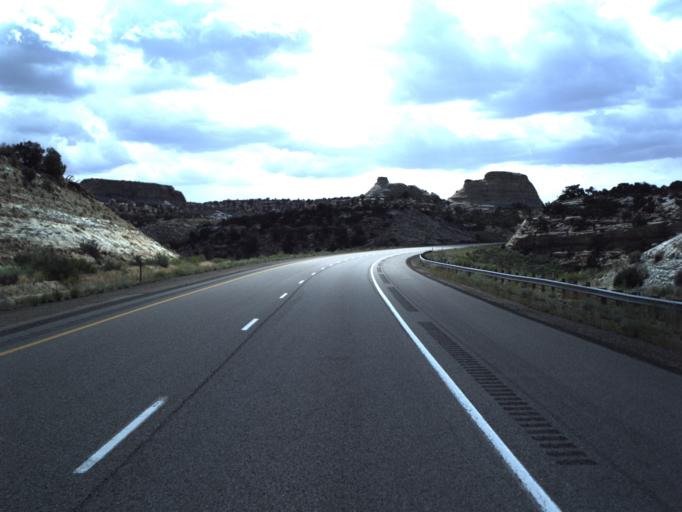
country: US
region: Utah
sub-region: Emery County
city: Ferron
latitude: 38.8575
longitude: -110.8706
